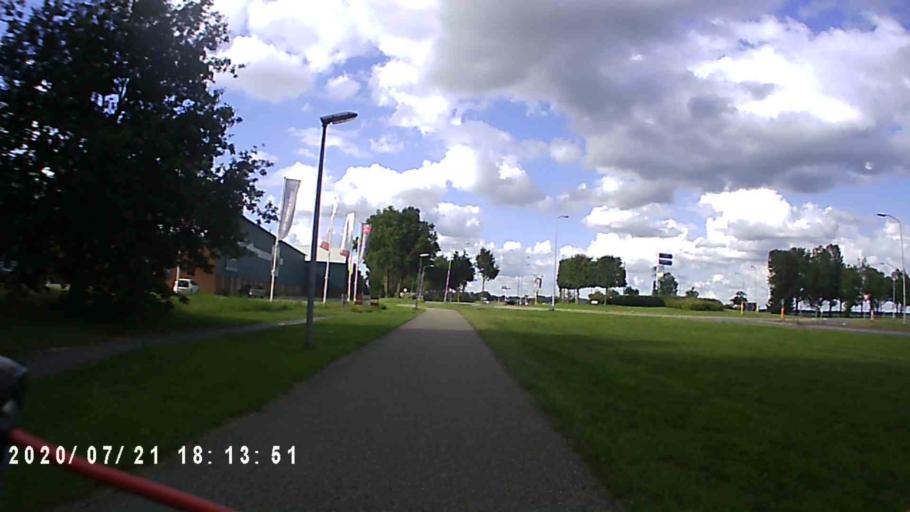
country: NL
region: Groningen
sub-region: Gemeente Hoogezand-Sappemeer
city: Hoogezand
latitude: 53.1702
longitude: 6.7557
